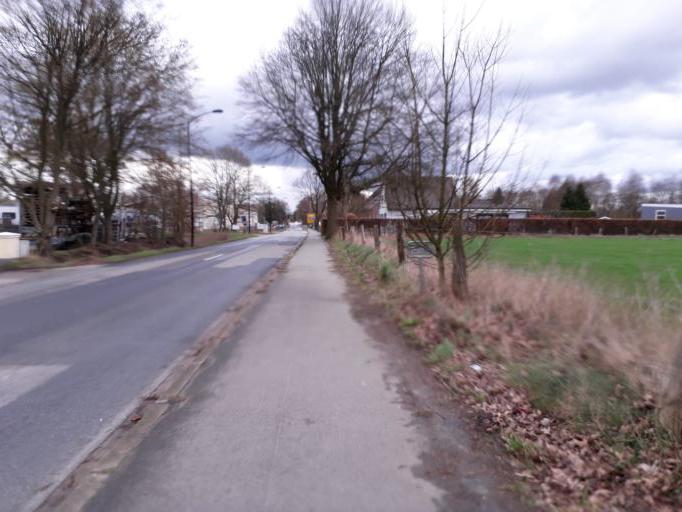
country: DE
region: Schleswig-Holstein
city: Glinde
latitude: 53.5651
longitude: 10.2147
